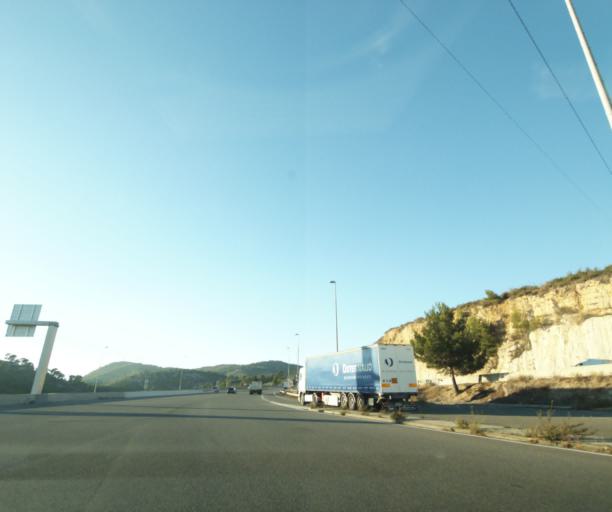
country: FR
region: Provence-Alpes-Cote d'Azur
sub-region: Departement des Bouches-du-Rhone
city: La Ciotat
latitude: 43.2058
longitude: 5.5894
